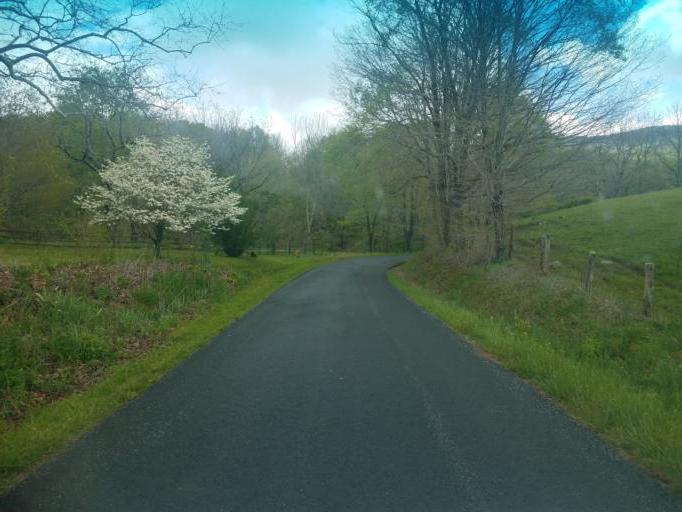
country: US
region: Virginia
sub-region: Smyth County
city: Atkins
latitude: 36.9557
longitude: -81.4010
